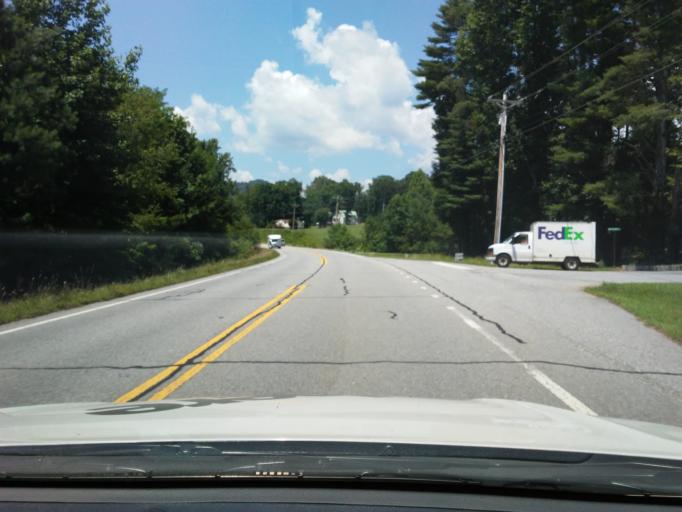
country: US
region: Georgia
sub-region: Towns County
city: Hiawassee
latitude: 34.9706
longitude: -83.7395
